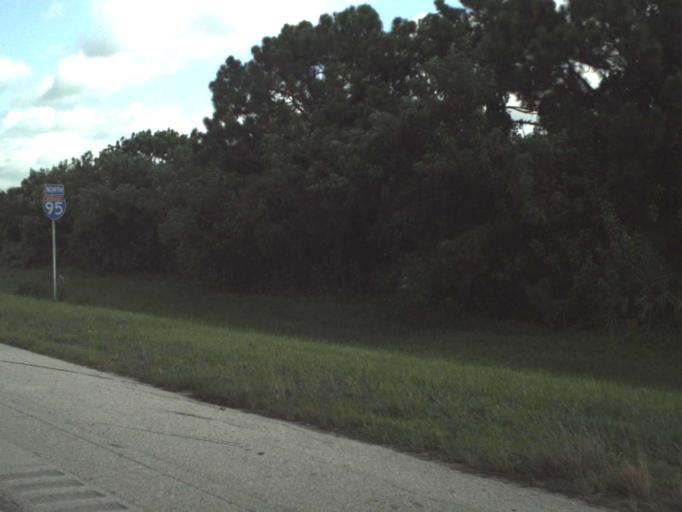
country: US
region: Florida
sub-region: Palm Beach County
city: Limestone Creek
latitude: 26.9452
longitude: -80.1556
